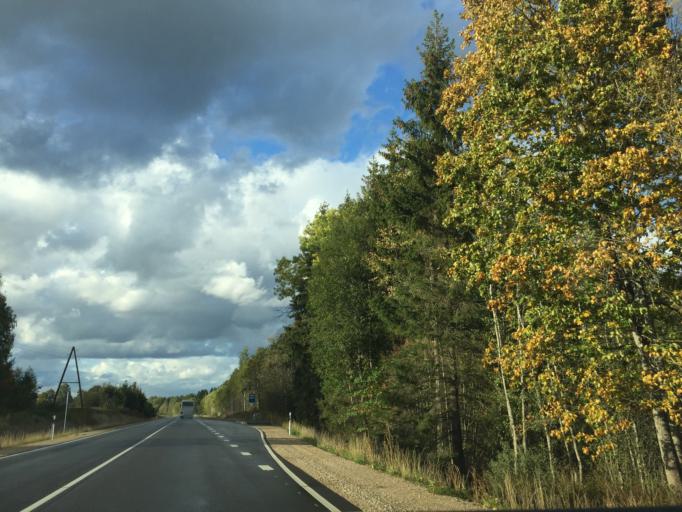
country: LV
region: Ligatne
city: Ligatne
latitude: 57.1395
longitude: 25.0814
